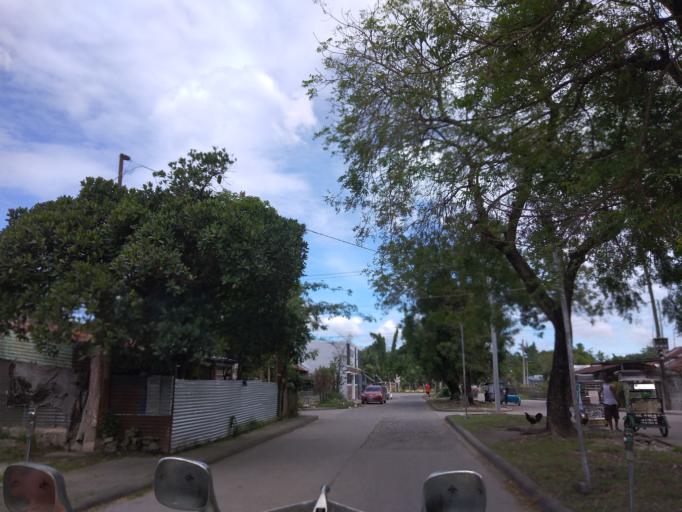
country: PH
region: Central Luzon
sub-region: Province of Pampanga
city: Pandacaqui
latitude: 15.1775
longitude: 120.6548
